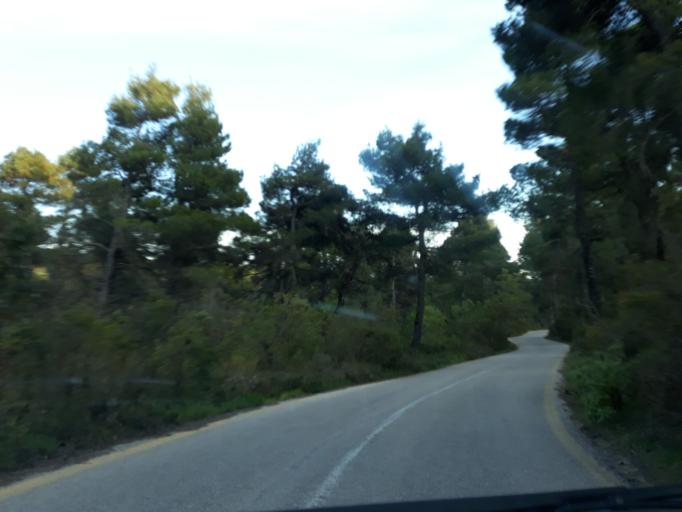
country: GR
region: Attica
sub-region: Nomarchia Anatolikis Attikis
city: Afidnes
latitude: 38.2112
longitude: 23.7901
